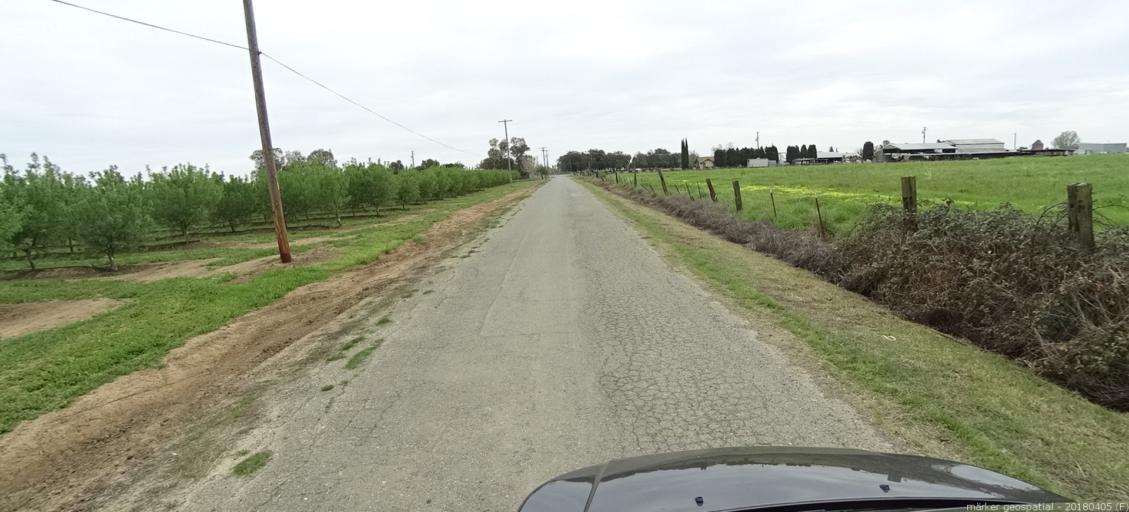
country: US
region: California
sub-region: Sacramento County
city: Galt
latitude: 38.2800
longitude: -121.3112
